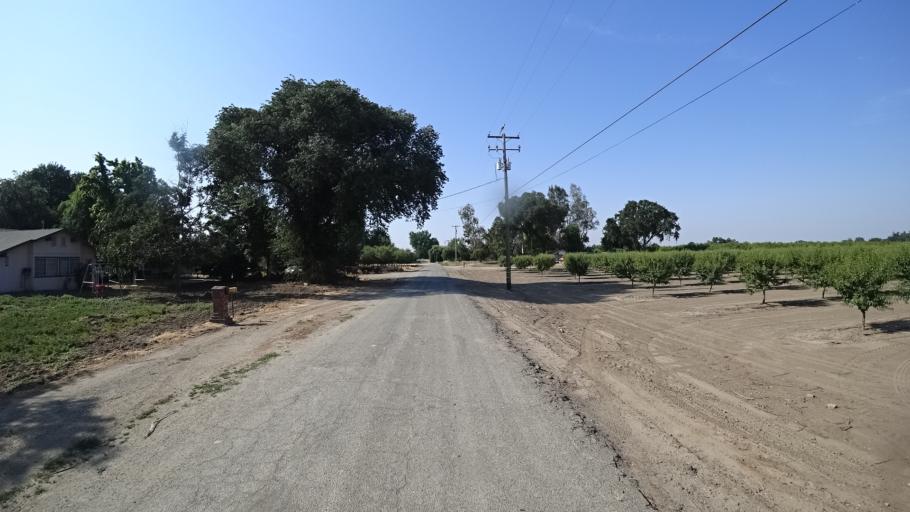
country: US
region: California
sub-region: Kings County
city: Lemoore
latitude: 36.3520
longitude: -119.8430
